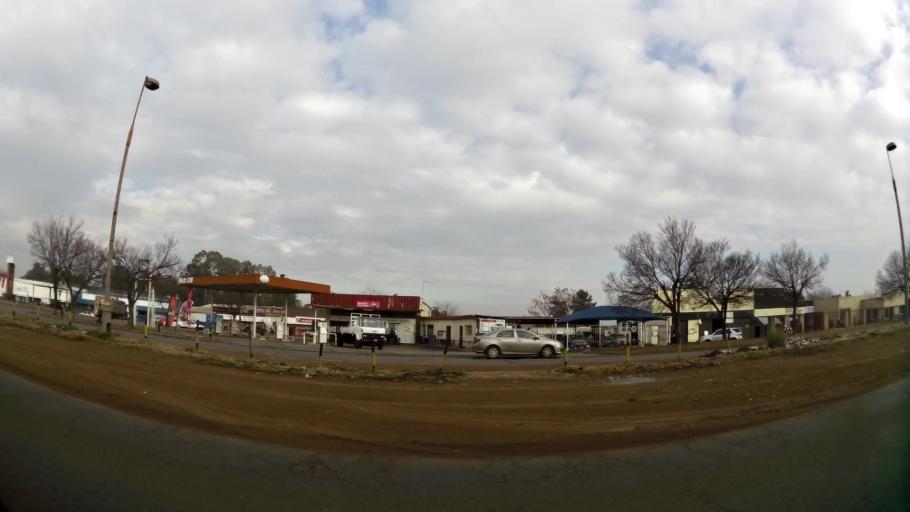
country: ZA
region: Gauteng
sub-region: Sedibeng District Municipality
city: Vanderbijlpark
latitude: -26.6912
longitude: 27.8133
